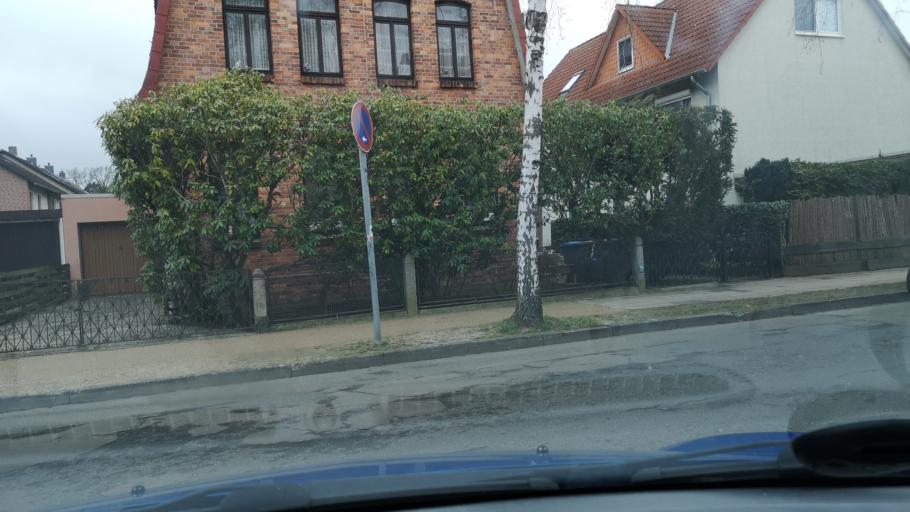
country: DE
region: Lower Saxony
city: Celle
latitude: 52.6135
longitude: 10.0455
